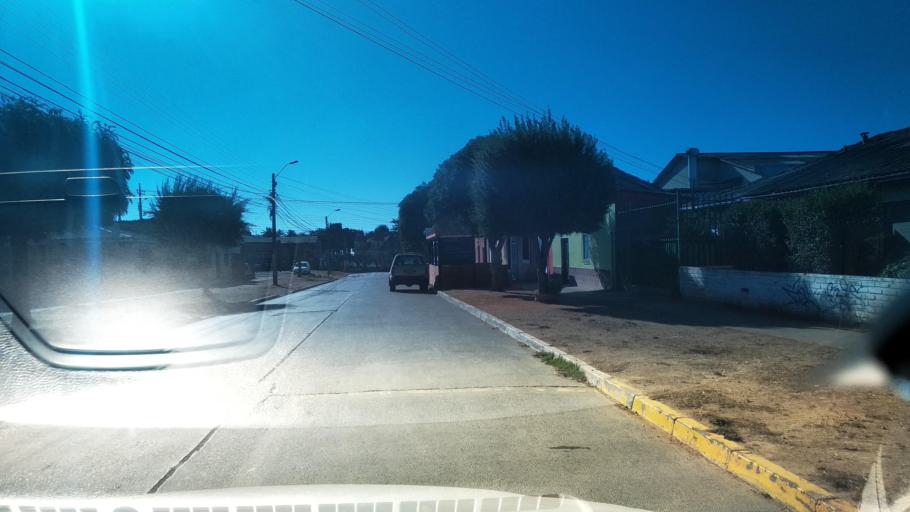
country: CL
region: O'Higgins
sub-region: Provincia de Colchagua
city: Santa Cruz
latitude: -34.3892
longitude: -72.0078
